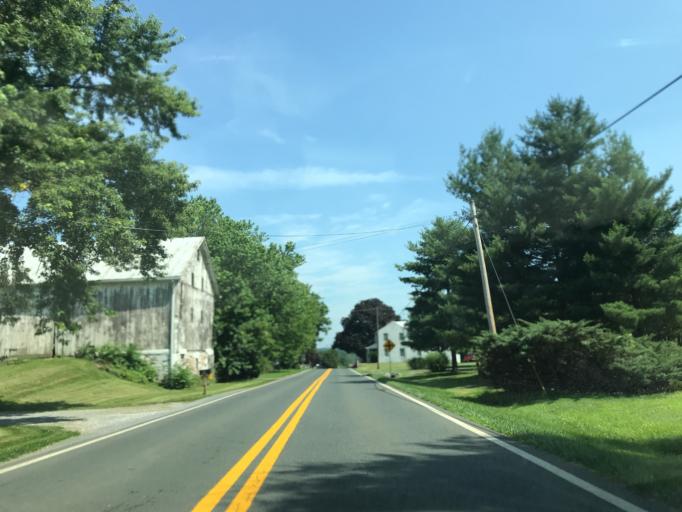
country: US
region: Maryland
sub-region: Carroll County
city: Taneytown
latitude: 39.6355
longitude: -77.1551
